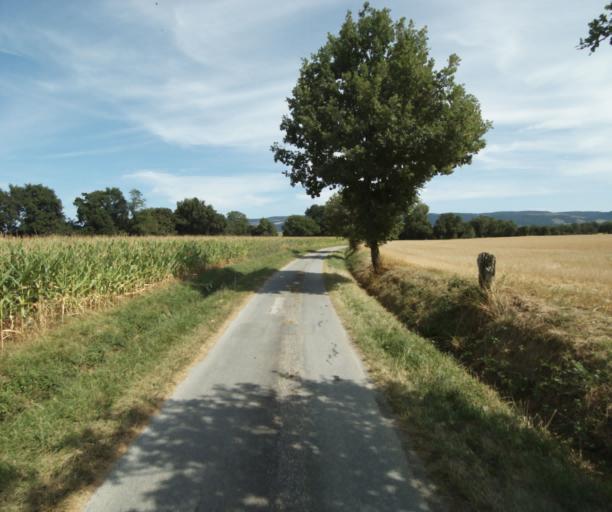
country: FR
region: Midi-Pyrenees
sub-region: Departement du Tarn
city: Soreze
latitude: 43.5133
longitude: 2.0681
